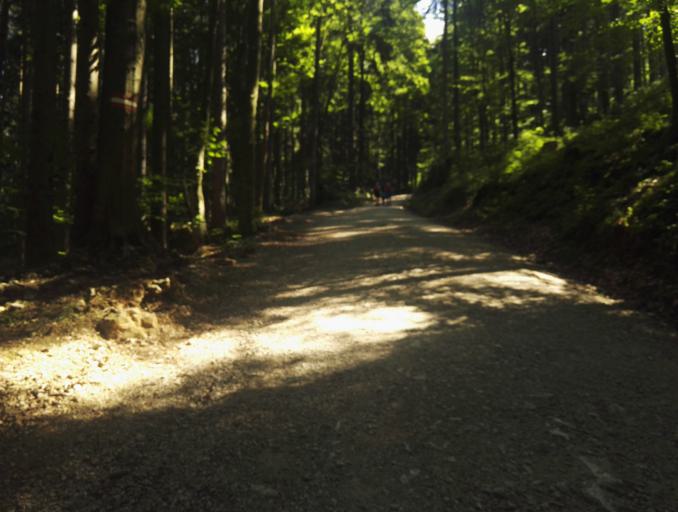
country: AT
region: Styria
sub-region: Politischer Bezirk Graz-Umgebung
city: Rothelstein
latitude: 47.3404
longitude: 15.3879
